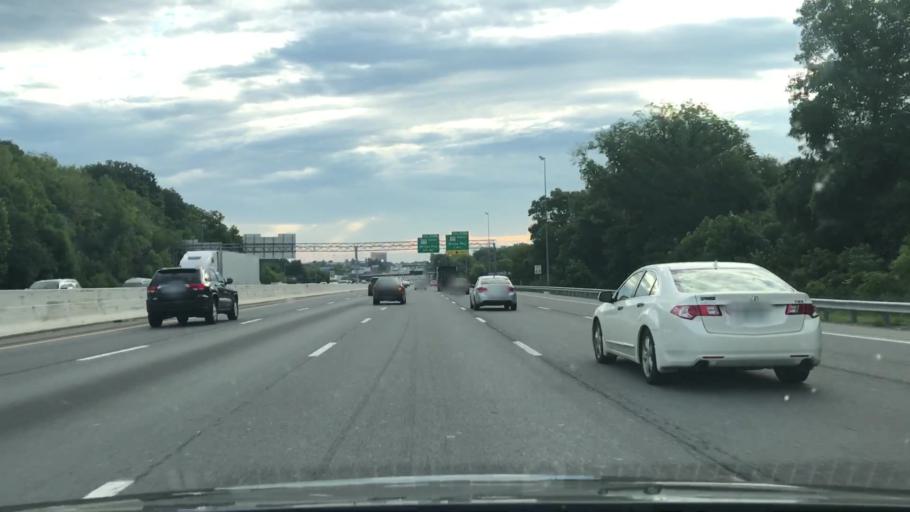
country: US
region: Tennessee
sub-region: Davidson County
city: Nashville
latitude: 36.1403
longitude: -86.7193
